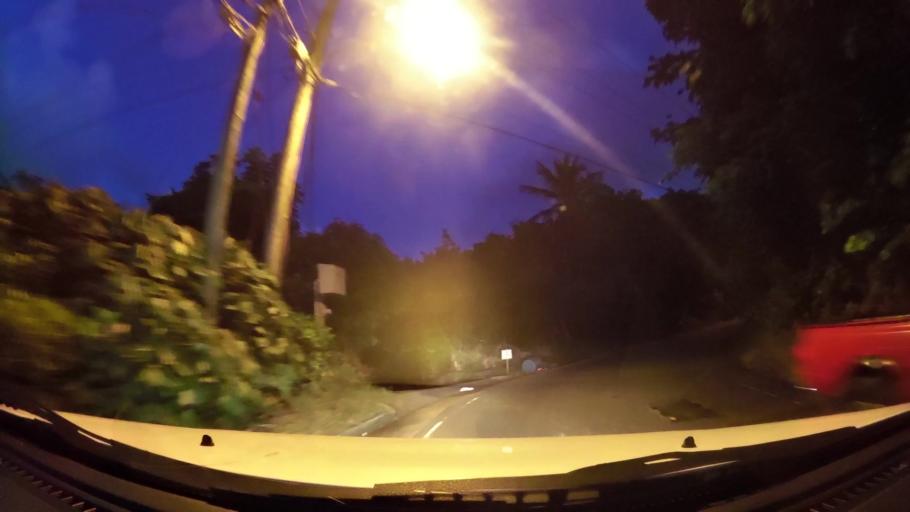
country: LC
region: Castries Quarter
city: Bisee
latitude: 14.0274
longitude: -60.9441
